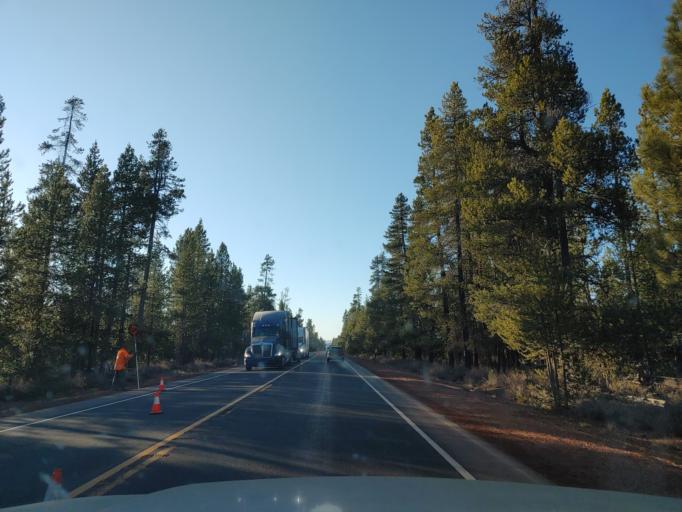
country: US
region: Oregon
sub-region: Deschutes County
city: La Pine
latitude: 43.3831
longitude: -121.8037
